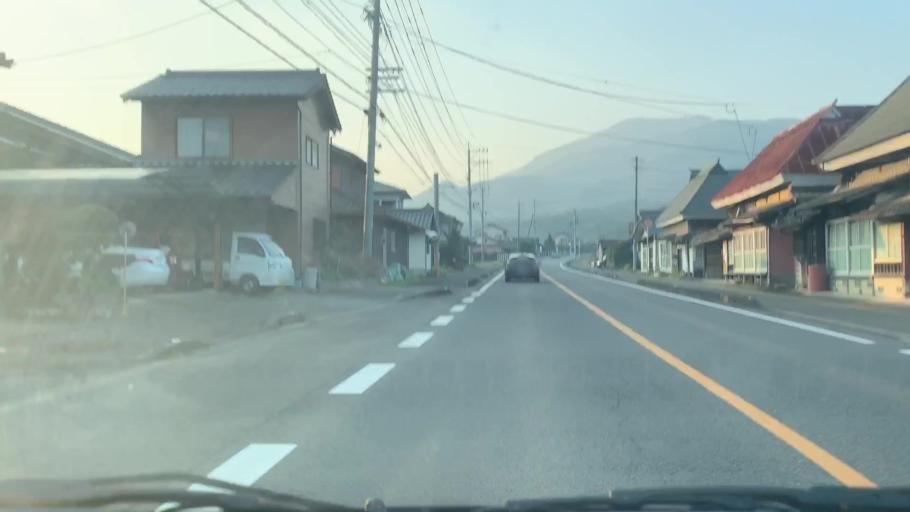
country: JP
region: Saga Prefecture
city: Takeocho-takeo
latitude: 33.2607
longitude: 130.0608
